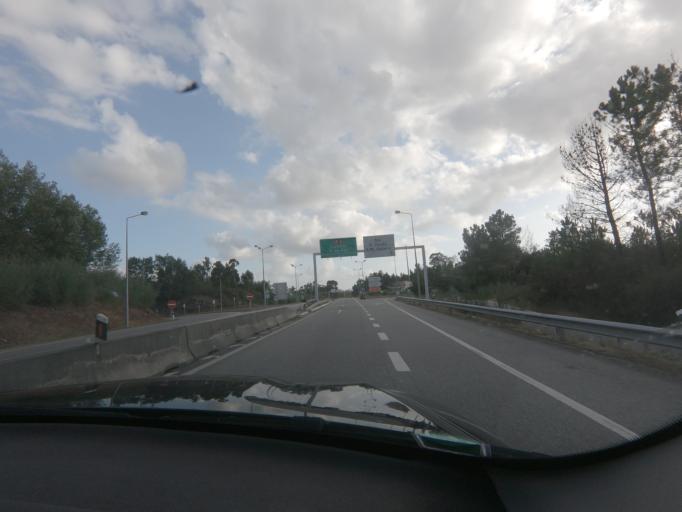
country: PT
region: Viseu
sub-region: Concelho de Tondela
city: Tondela
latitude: 40.5873
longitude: -8.0154
